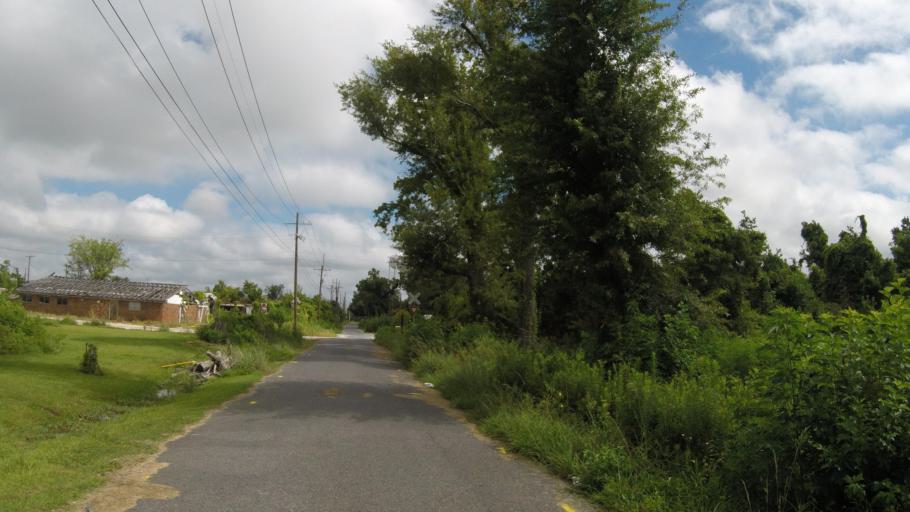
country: US
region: Louisiana
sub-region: Calcasieu Parish
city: Westlake
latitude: 30.2394
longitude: -93.2497
